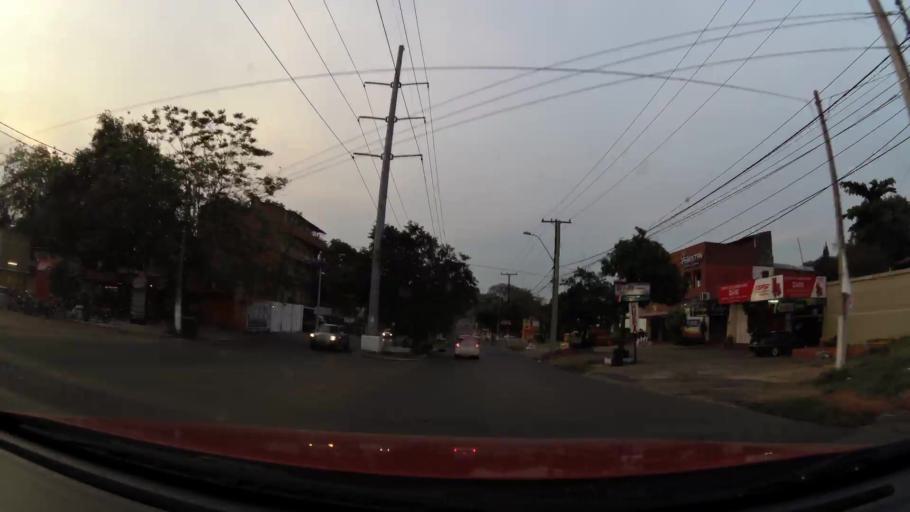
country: PY
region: Central
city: Lambare
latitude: -25.3329
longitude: -57.6256
